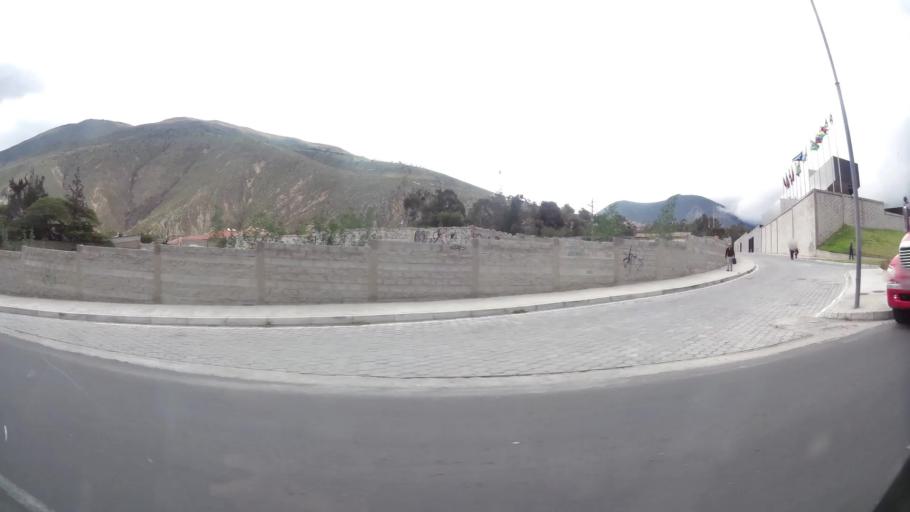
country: EC
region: Pichincha
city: Quito
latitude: -0.0057
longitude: -78.4531
